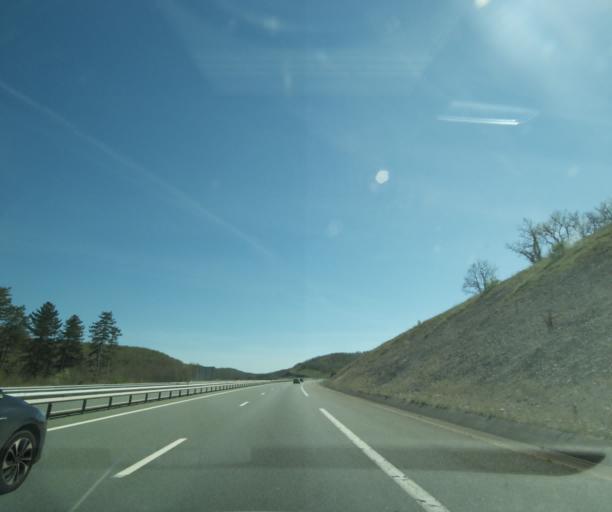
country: FR
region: Midi-Pyrenees
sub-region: Departement du Lot
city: Le Vigan
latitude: 44.7860
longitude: 1.5292
